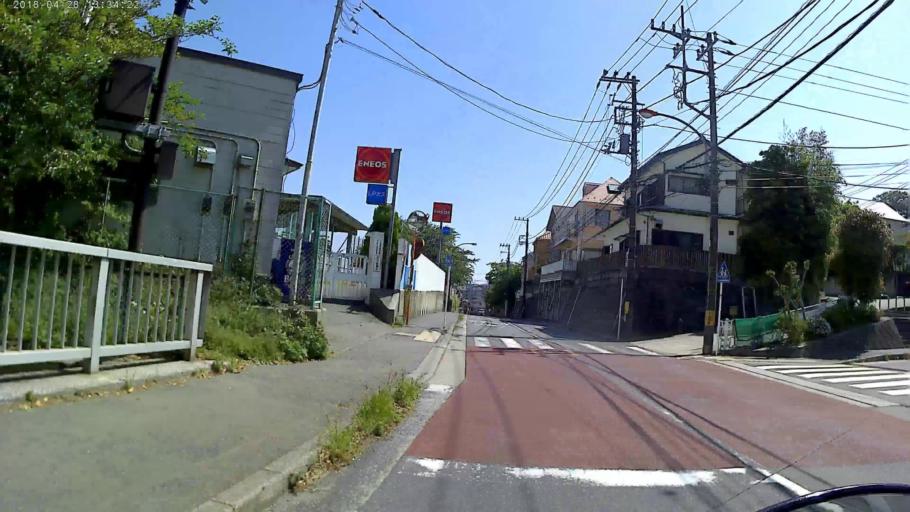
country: JP
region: Kanagawa
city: Yokosuka
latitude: 35.2176
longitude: 139.6930
